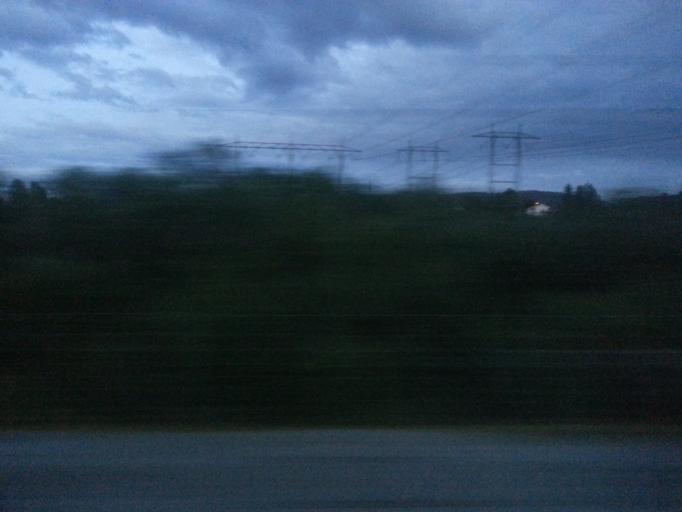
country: NO
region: Akershus
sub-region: Sorum
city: Frogner
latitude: 60.0082
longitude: 11.0998
